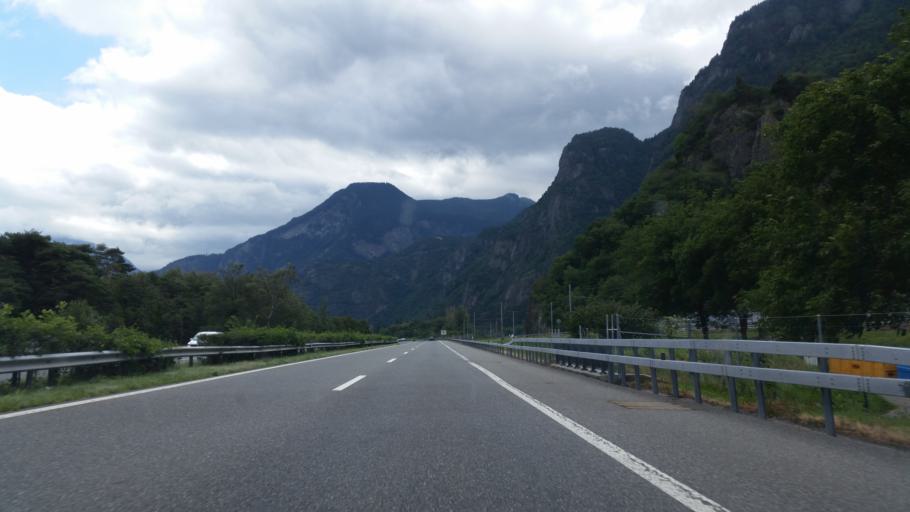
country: CH
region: Valais
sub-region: Saint-Maurice District
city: Vernayaz
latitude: 46.1577
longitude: 7.0316
